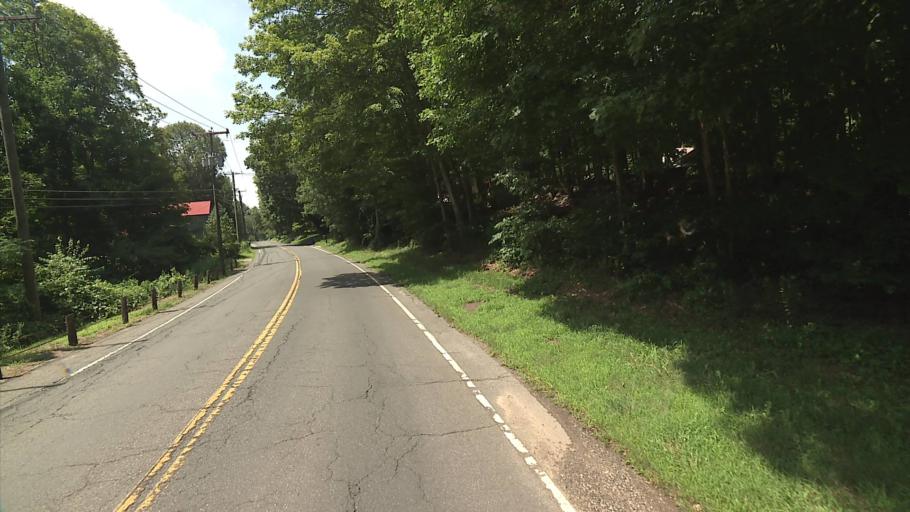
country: US
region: Connecticut
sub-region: Tolland County
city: South Coventry
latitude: 41.7617
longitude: -72.2798
